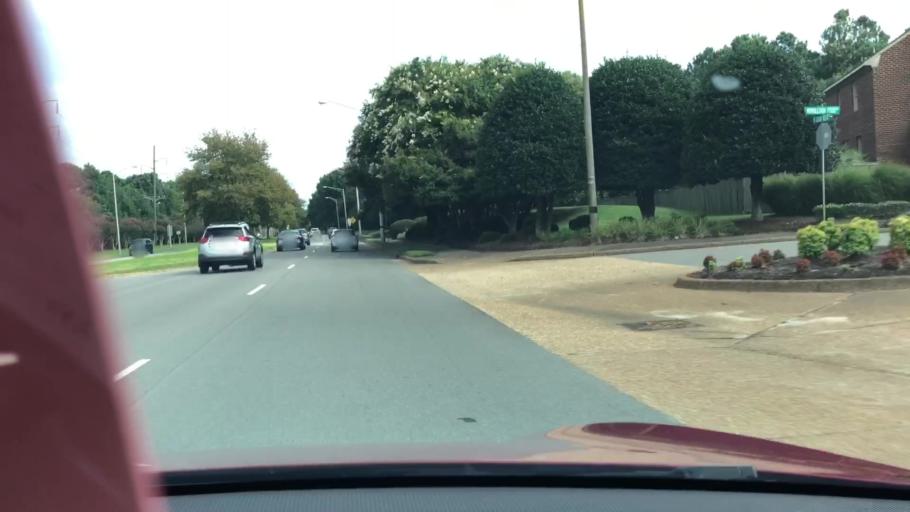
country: US
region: Virginia
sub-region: City of Virginia Beach
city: Virginia Beach
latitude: 36.8952
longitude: -76.0604
